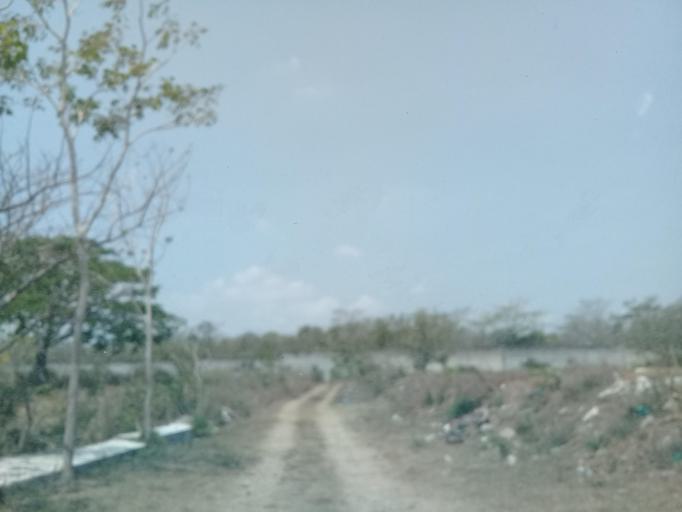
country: MX
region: Veracruz
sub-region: Veracruz
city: Hacienda Sotavento
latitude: 19.1340
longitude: -96.1837
